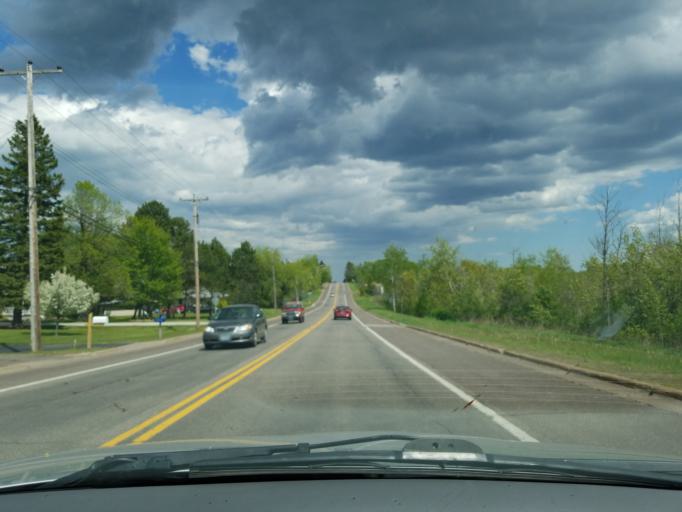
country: US
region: Minnesota
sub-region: Saint Louis County
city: Proctor
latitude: 46.7785
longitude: -92.1739
